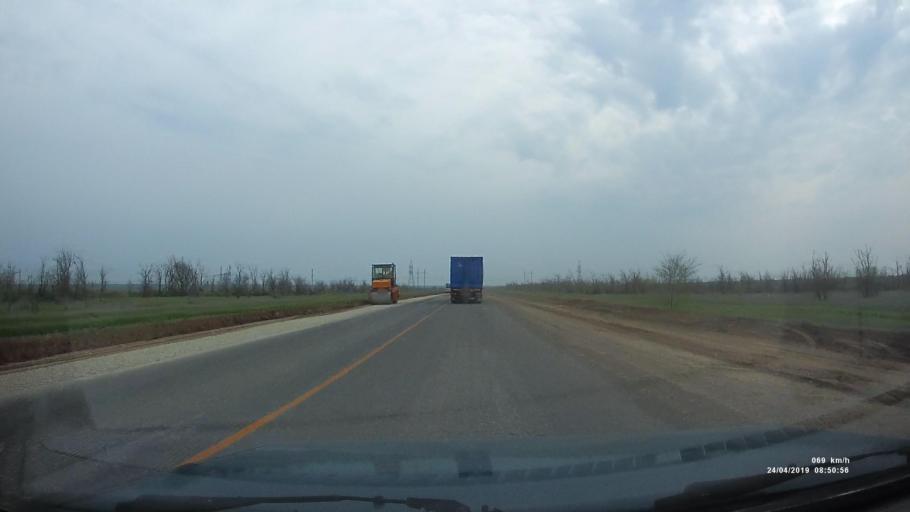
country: RU
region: Kalmykiya
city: Arshan'
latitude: 46.2644
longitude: 44.1435
